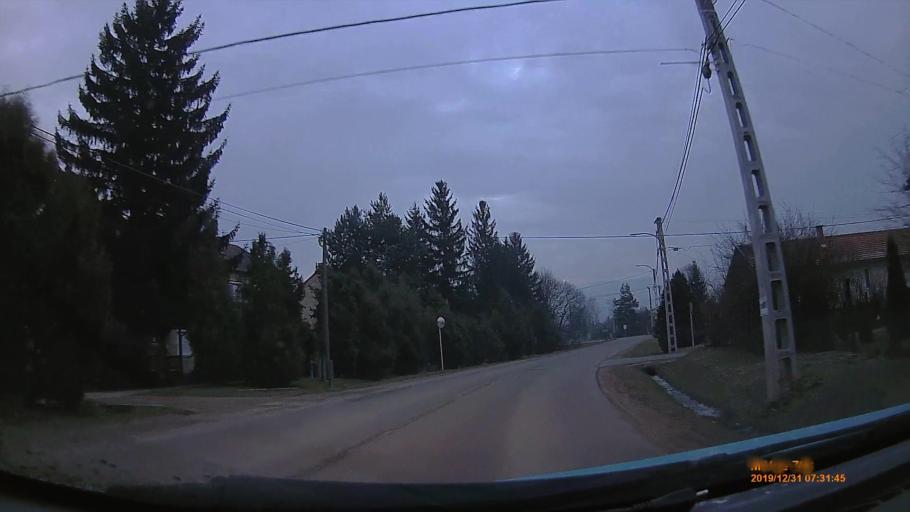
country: HU
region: Heves
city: Recsk
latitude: 47.9341
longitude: 20.1186
